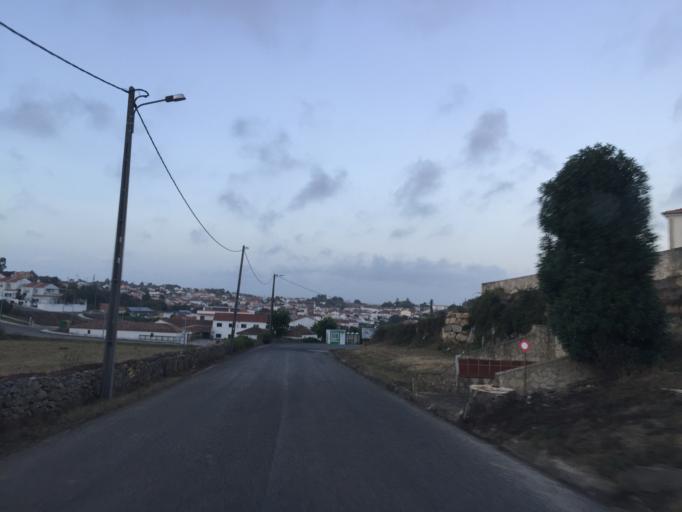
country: PT
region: Leiria
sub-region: Bombarral
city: Bombarral
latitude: 39.2835
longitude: -9.2224
